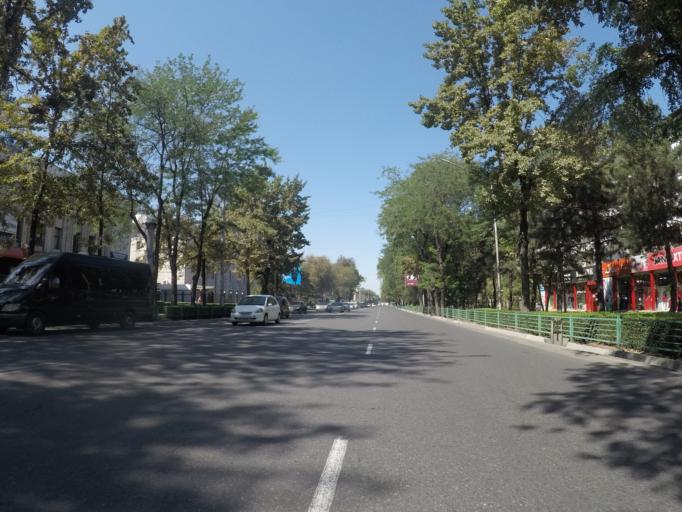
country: KG
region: Chuy
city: Bishkek
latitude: 42.8765
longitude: 74.5910
